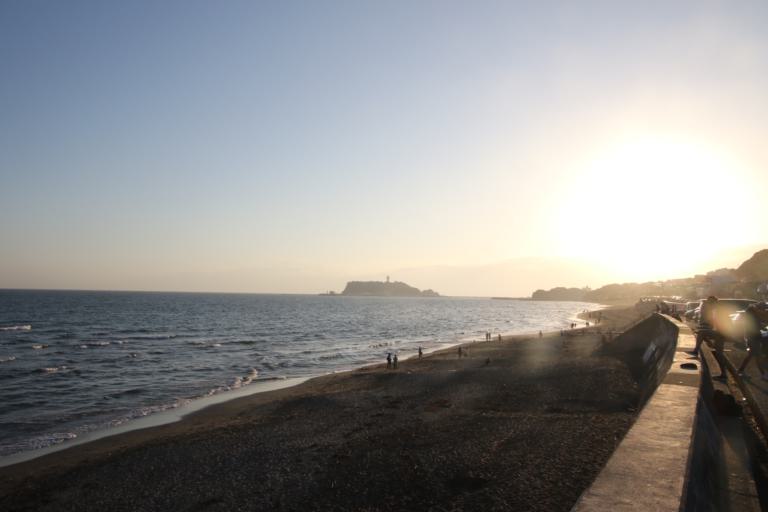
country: JP
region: Kanagawa
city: Kamakura
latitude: 35.3049
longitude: 139.5115
